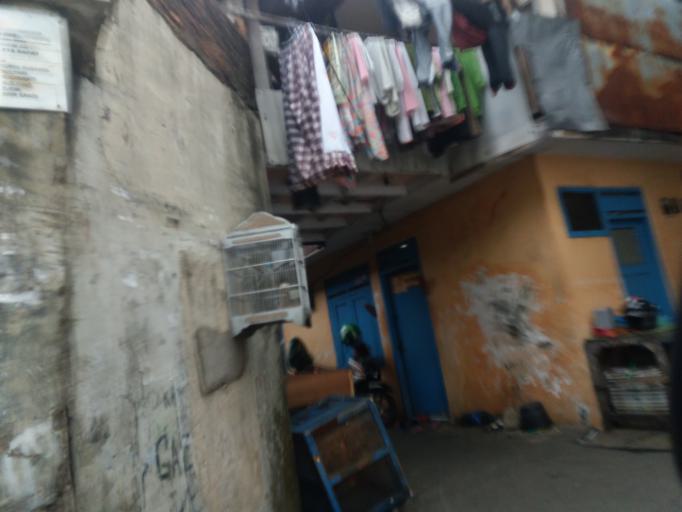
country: ID
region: Jakarta Raya
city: Jakarta
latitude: -6.1458
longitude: 106.8217
